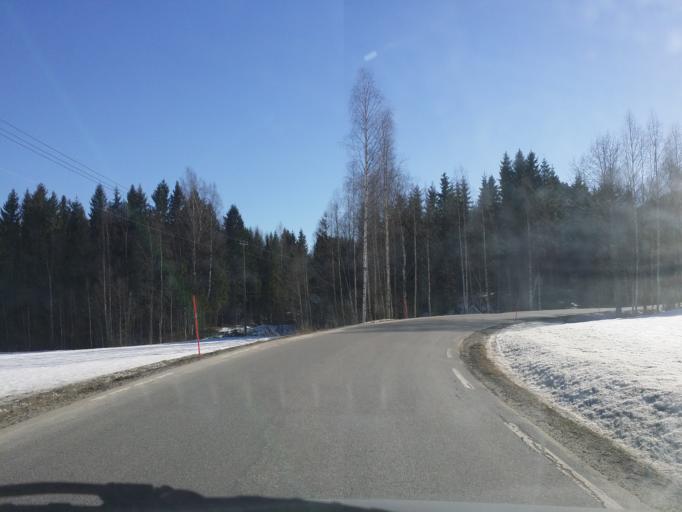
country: NO
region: Buskerud
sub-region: Ringerike
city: Honefoss
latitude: 60.3831
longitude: 10.0529
